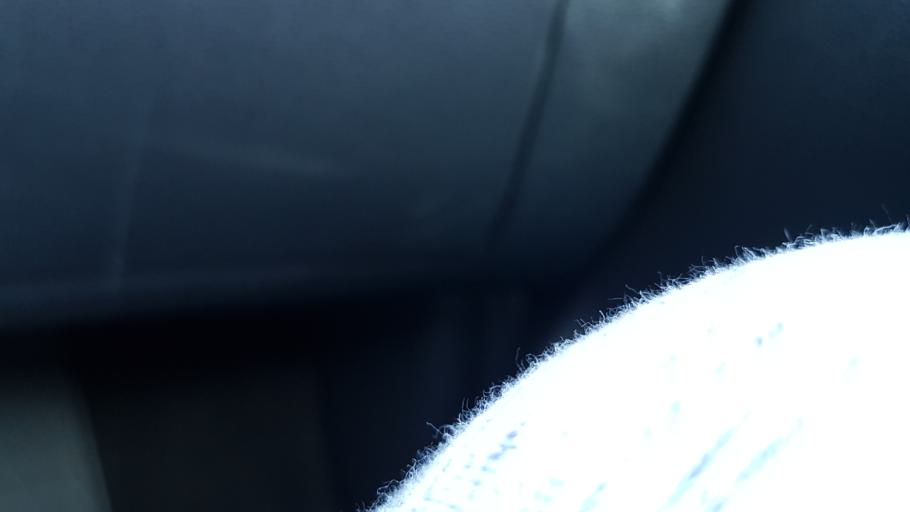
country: RO
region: Ilfov
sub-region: Comuna Fundeni-Dobroesti
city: Fundeni
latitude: 44.4402
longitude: 26.1456
